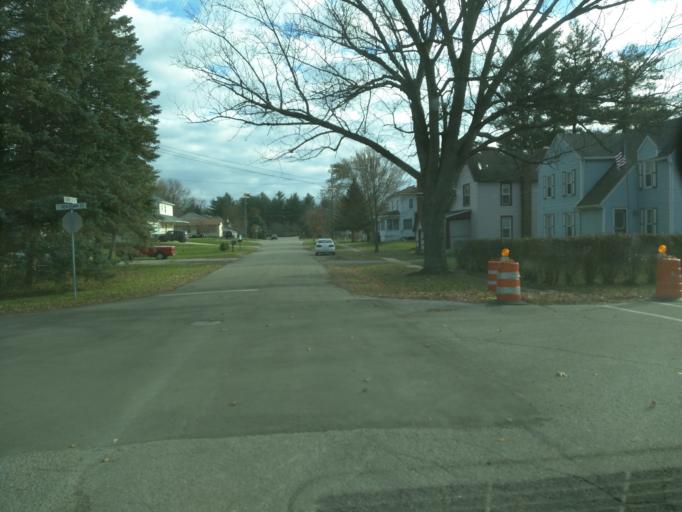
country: US
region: Michigan
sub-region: Livingston County
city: Fowlerville
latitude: 42.6596
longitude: -84.0666
